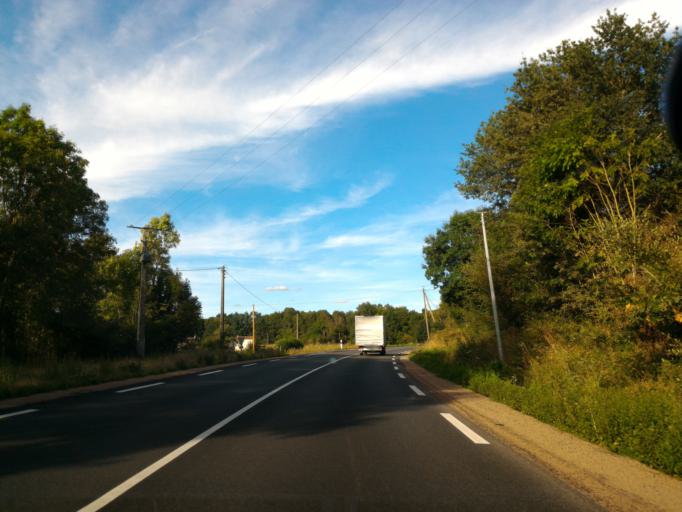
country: FR
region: Limousin
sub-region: Departement de la Haute-Vienne
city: Magnac-Laval
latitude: 46.1640
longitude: 1.1353
